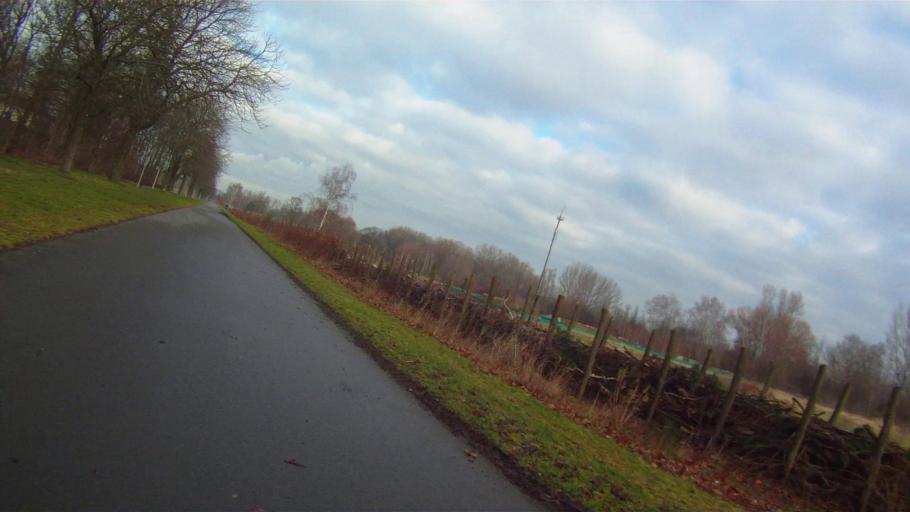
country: DE
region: Berlin
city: Oberschoneweide
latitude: 52.4688
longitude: 13.5274
